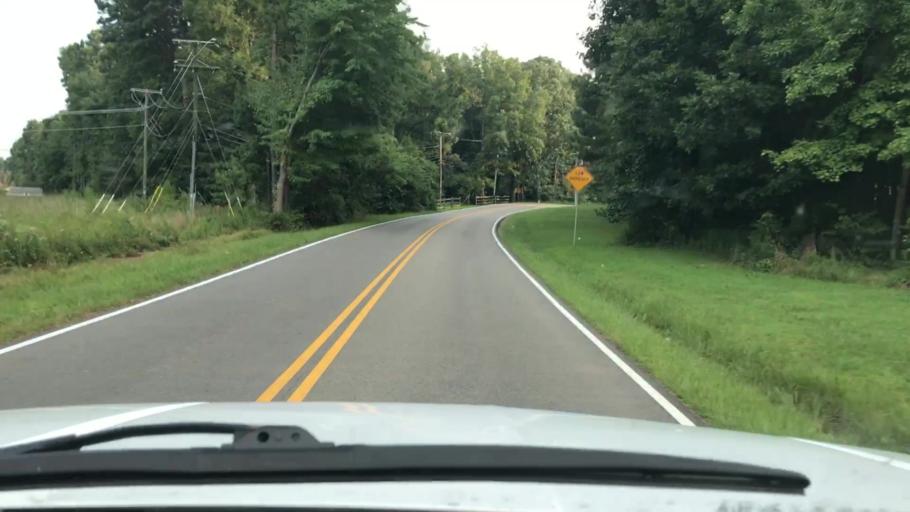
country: US
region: Virginia
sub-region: Chesterfield County
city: Chesterfield
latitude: 37.4356
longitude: -77.5254
